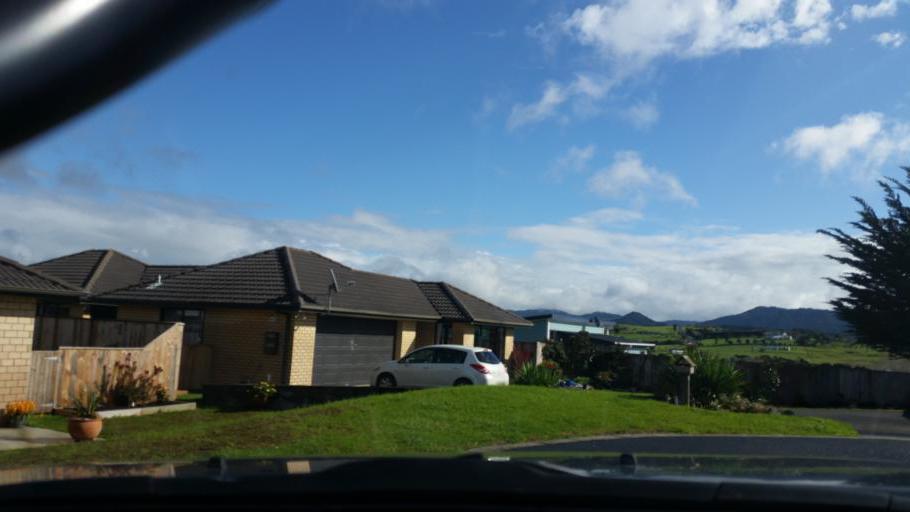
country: NZ
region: Auckland
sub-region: Auckland
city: Wellsford
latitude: -36.0866
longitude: 174.5781
